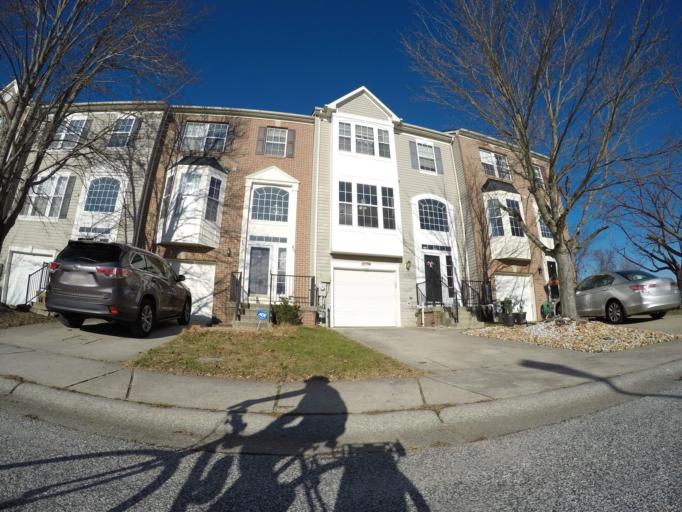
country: US
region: Maryland
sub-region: Howard County
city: Ellicott City
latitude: 39.3068
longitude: -76.8163
